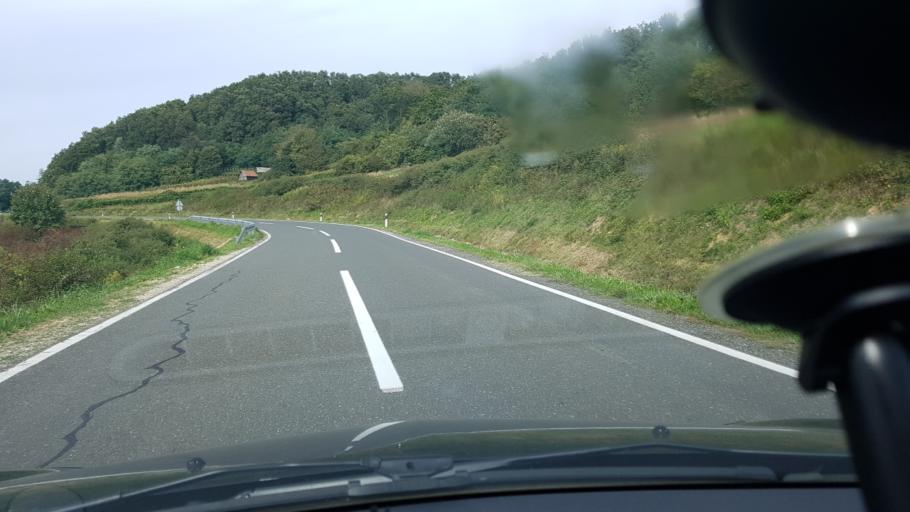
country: HR
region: Varazdinska
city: Ljubescica
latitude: 46.1107
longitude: 16.3567
